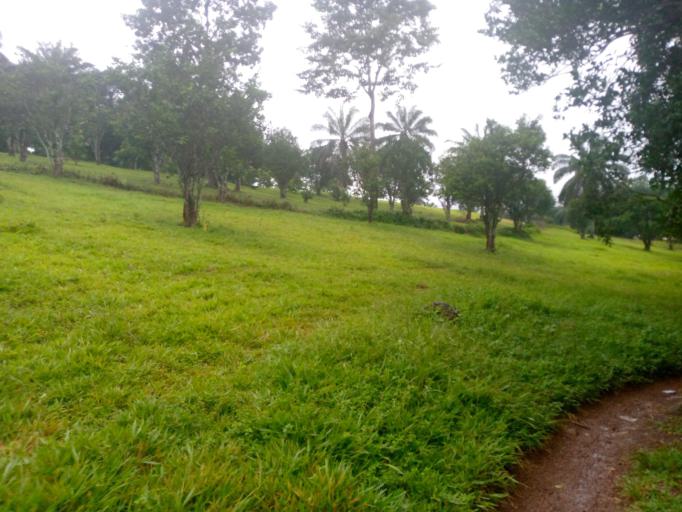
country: SL
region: Eastern Province
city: Kenema
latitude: 7.8780
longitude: -11.1758
